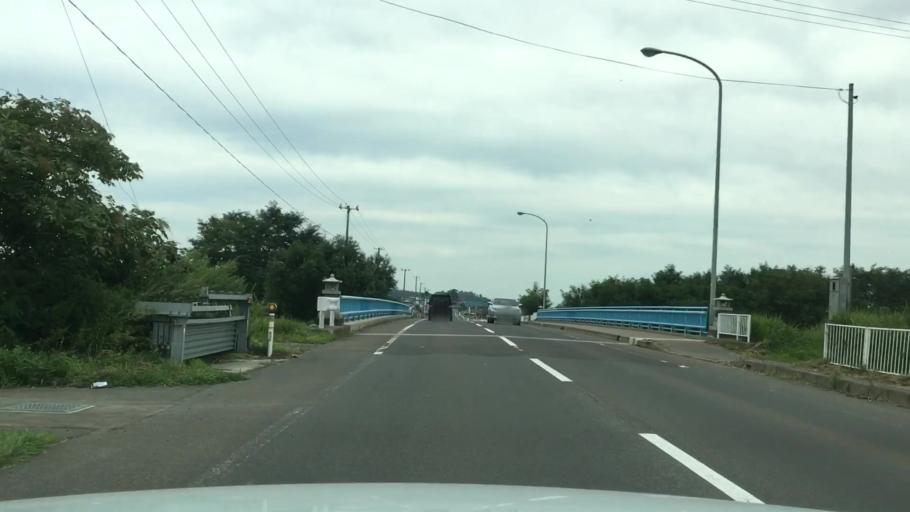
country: JP
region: Aomori
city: Hirosaki
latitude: 40.6368
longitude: 140.4484
